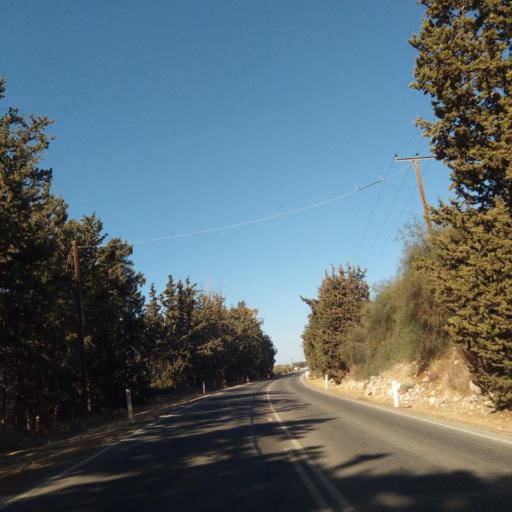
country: CY
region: Larnaka
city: Kolossi
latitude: 34.6554
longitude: 32.9259
